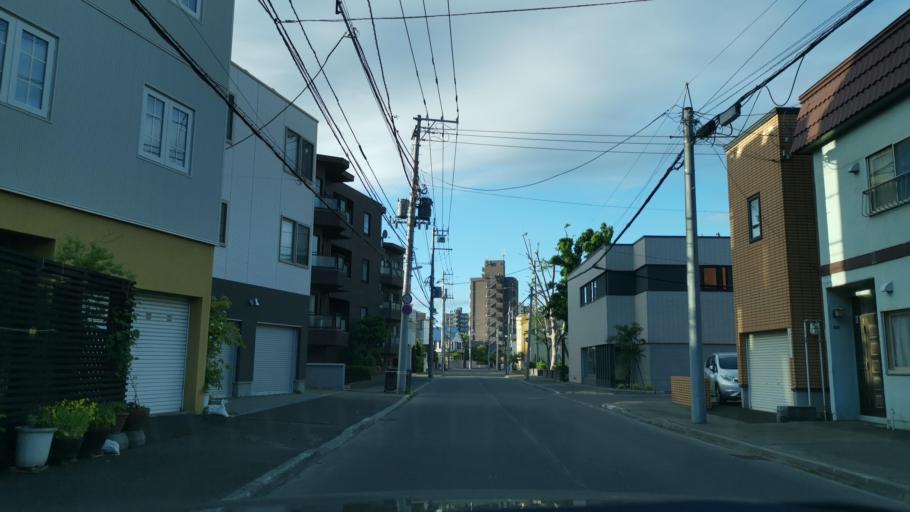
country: JP
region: Hokkaido
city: Sapporo
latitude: 43.0461
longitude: 141.3266
